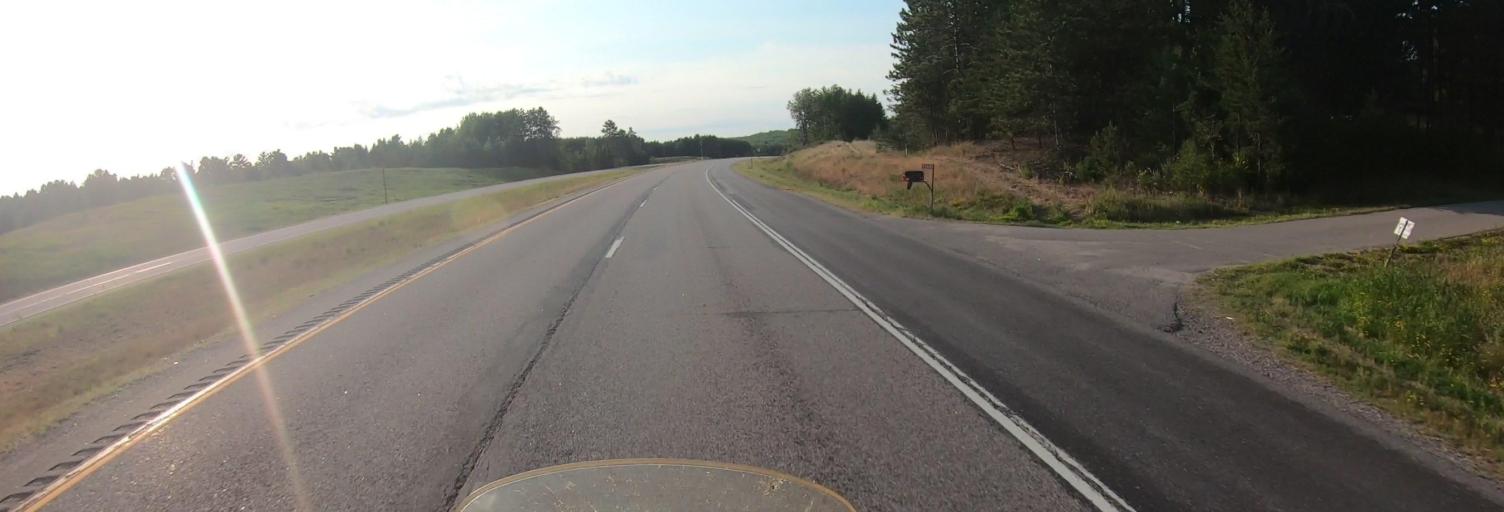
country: US
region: Minnesota
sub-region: Saint Louis County
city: Mountain Iron
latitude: 47.6725
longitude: -92.6325
